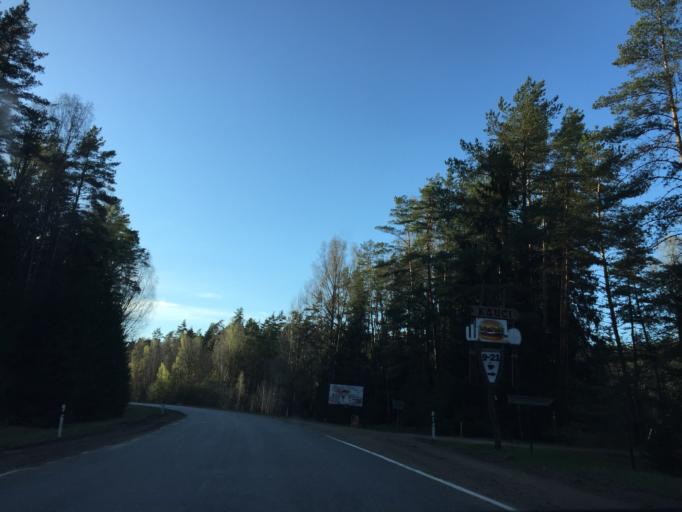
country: LV
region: Strenci
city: Seda
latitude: 57.6288
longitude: 25.7415
